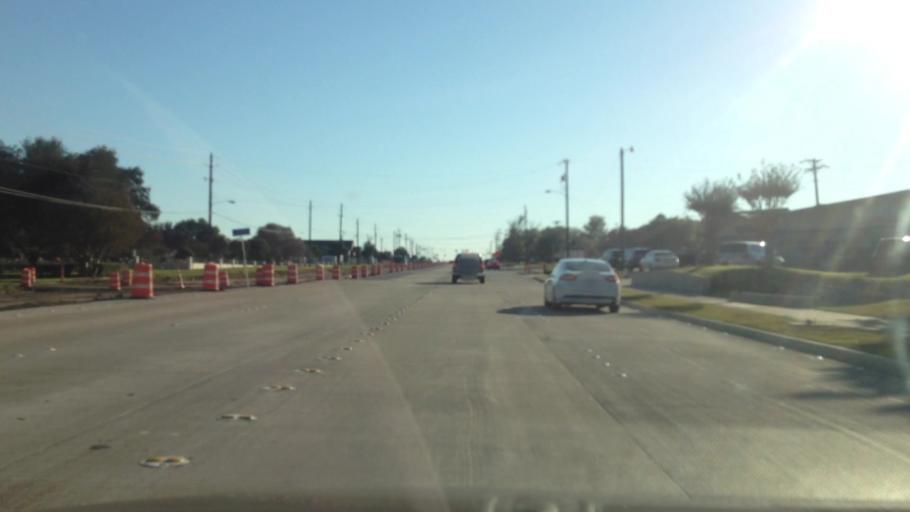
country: US
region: Texas
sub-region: Tarrant County
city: Colleyville
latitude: 32.8963
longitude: -97.1454
